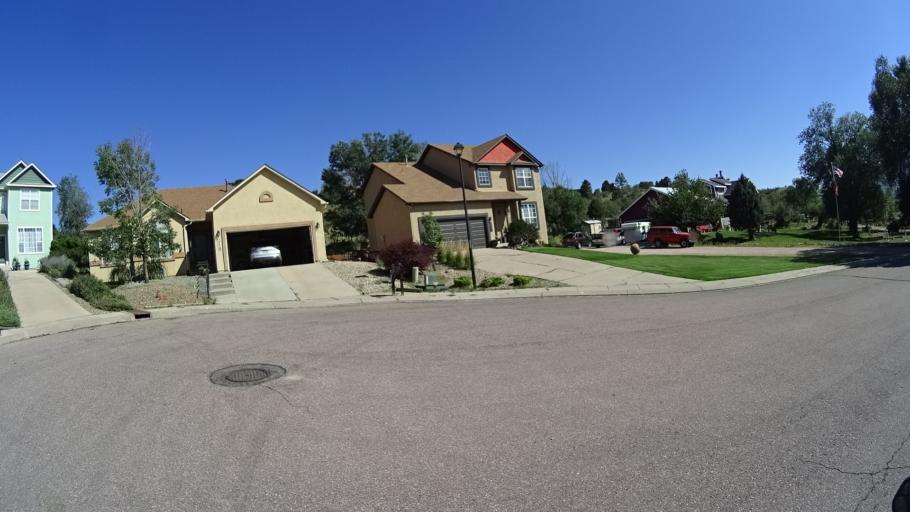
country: US
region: Colorado
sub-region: El Paso County
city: Colorado Springs
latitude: 38.8539
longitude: -104.8469
